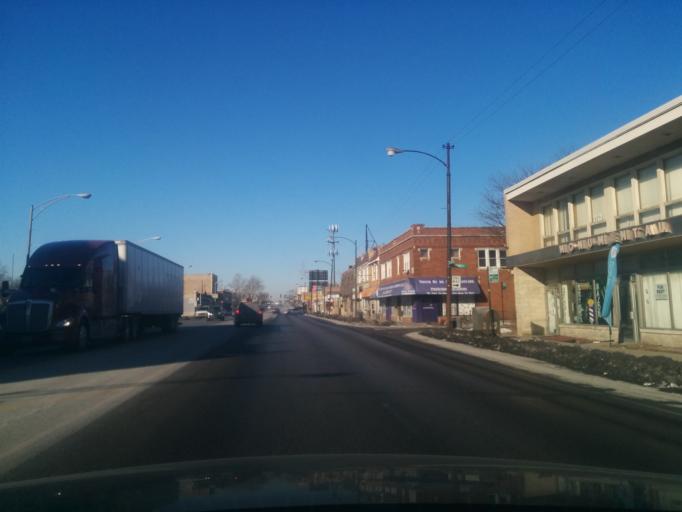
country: US
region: Illinois
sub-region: Cook County
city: Oak Park
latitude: 41.9092
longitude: -87.7784
